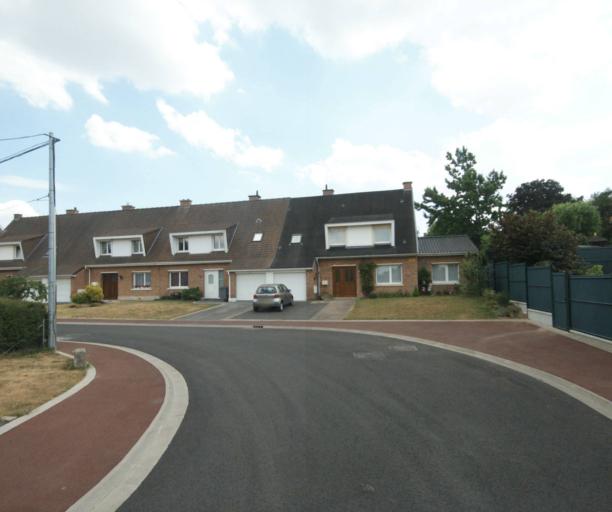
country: FR
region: Nord-Pas-de-Calais
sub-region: Departement du Nord
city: Neuville-en-Ferrain
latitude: 50.7481
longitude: 3.1619
